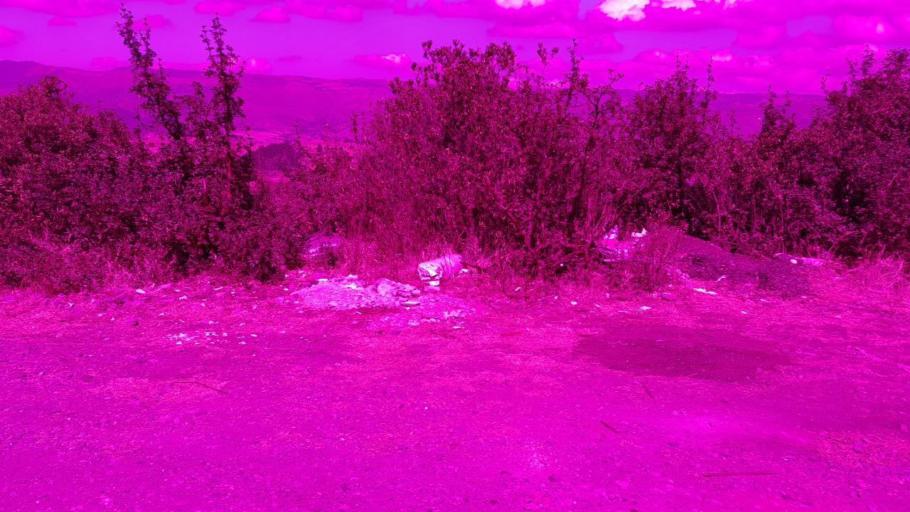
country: PE
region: Cusco
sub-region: Provincia de Cusco
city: Cusco
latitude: -13.4974
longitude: -71.9259
